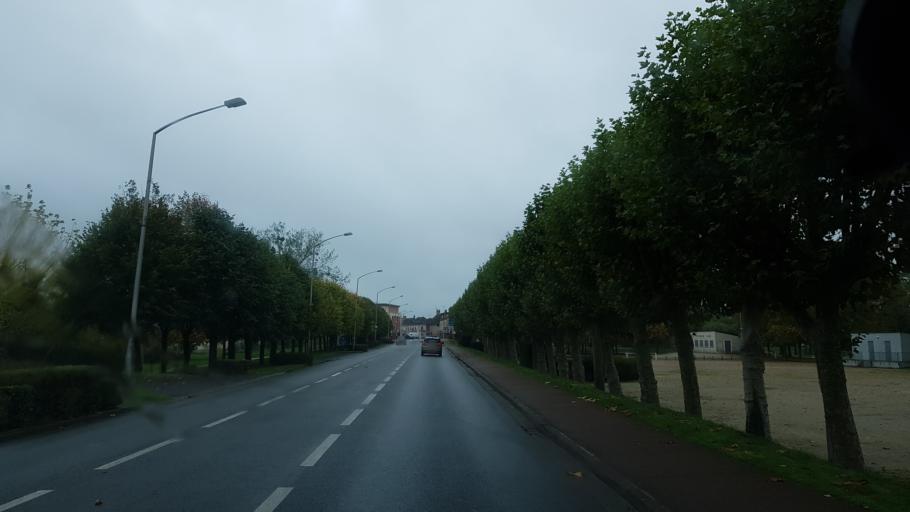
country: FR
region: Centre
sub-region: Departement du Loir-et-Cher
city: Salbris
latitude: 47.4294
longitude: 2.0510
